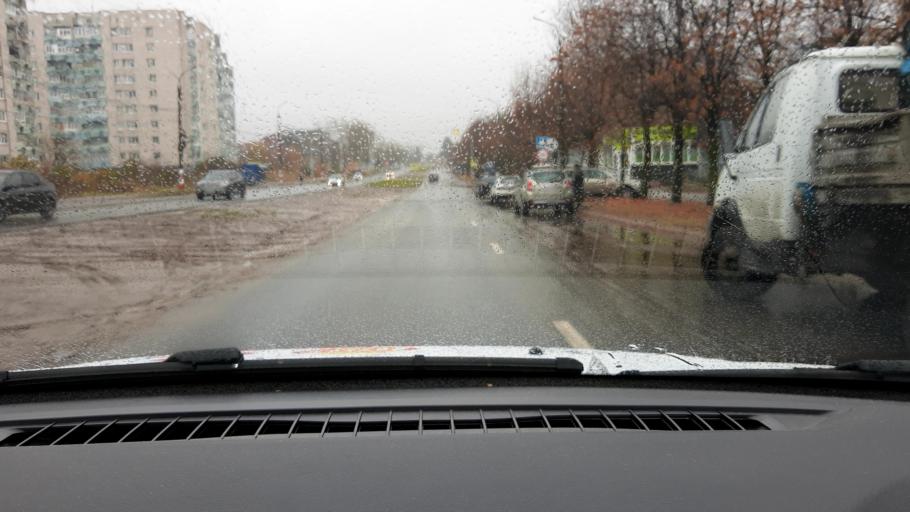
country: RU
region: Nizjnij Novgorod
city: Dzerzhinsk
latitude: 56.2463
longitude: 43.4233
